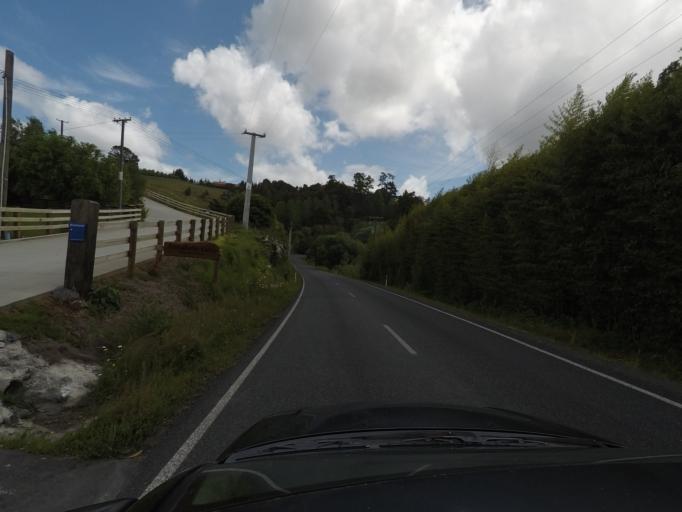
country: NZ
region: Auckland
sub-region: Auckland
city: Warkworth
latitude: -36.5054
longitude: 174.6463
